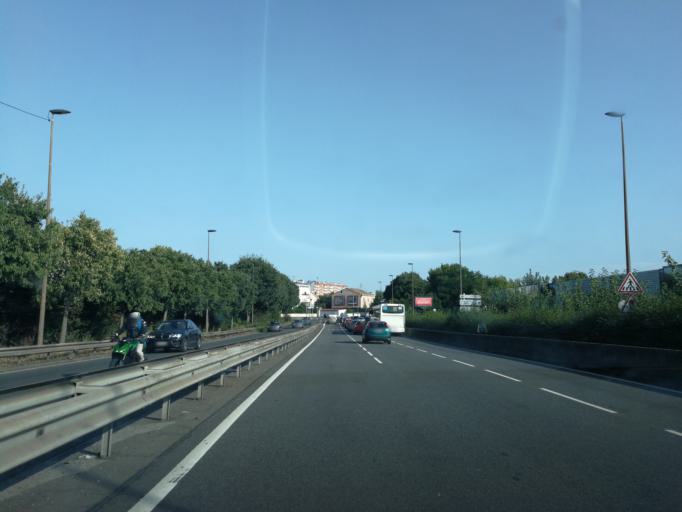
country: FR
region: Midi-Pyrenees
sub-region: Departement de la Haute-Garonne
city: Toulouse
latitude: 43.6226
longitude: 1.4233
